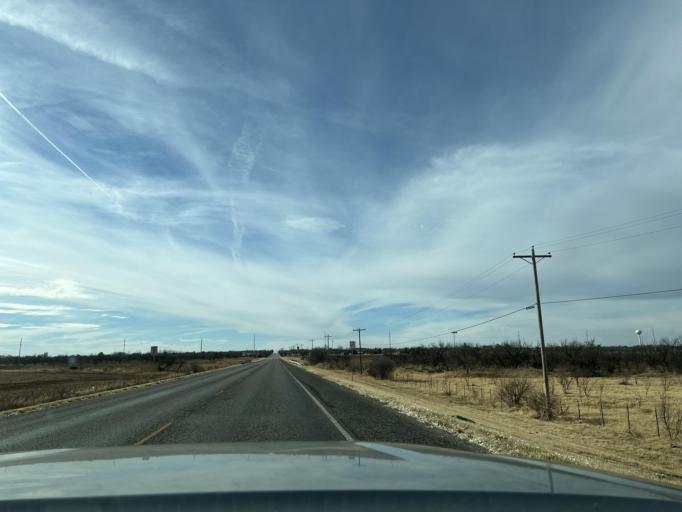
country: US
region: Texas
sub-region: Jones County
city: Anson
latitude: 32.7515
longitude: -99.8810
